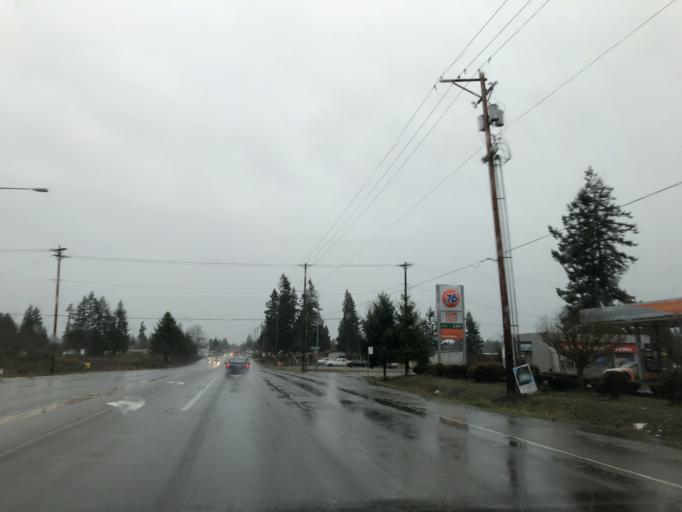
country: US
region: Washington
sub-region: Pierce County
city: Spanaway
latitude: 47.0792
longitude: -122.4292
